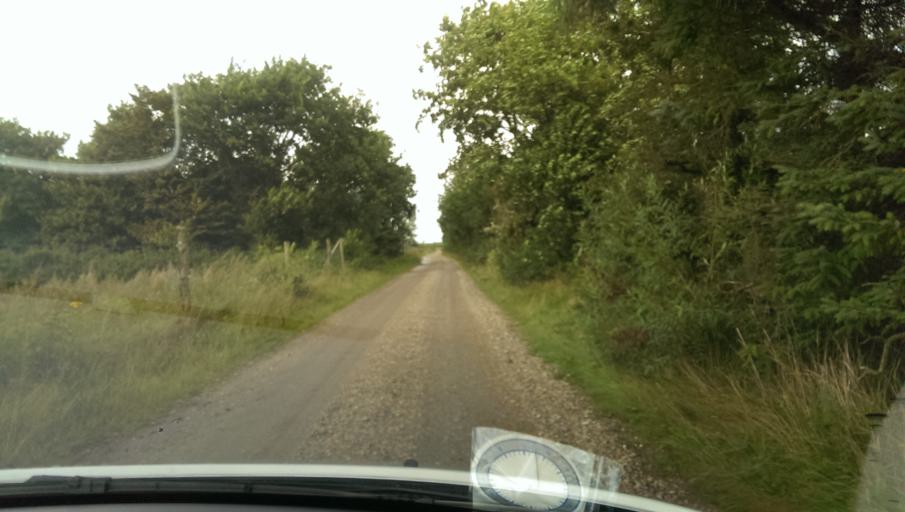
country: DK
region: South Denmark
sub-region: Varde Kommune
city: Varde
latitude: 55.6072
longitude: 8.4495
